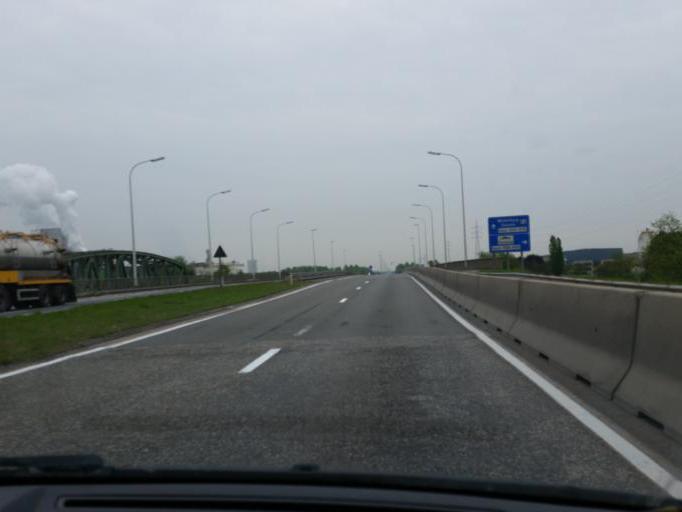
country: BE
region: Flanders
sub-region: Provincie Oost-Vlaanderen
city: Lochristi
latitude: 51.1356
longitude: 3.7914
